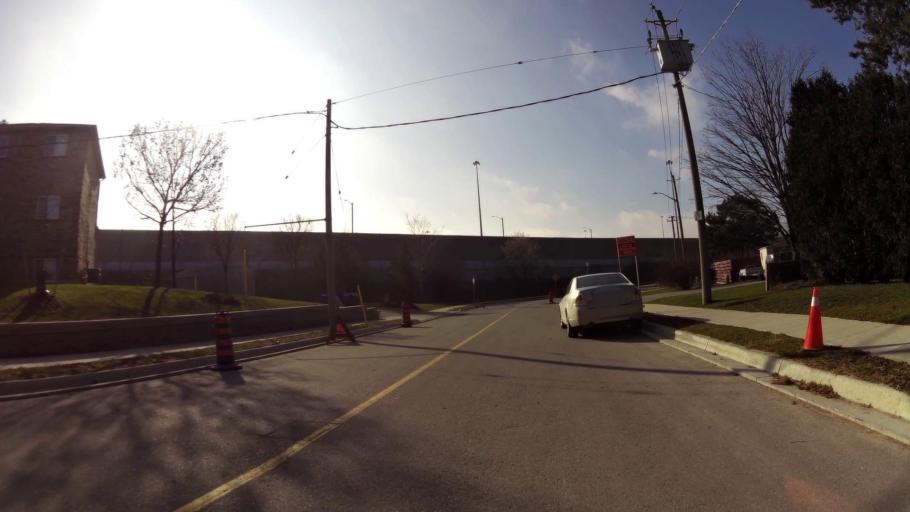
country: CA
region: Ontario
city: Kitchener
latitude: 43.4292
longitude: -80.4824
